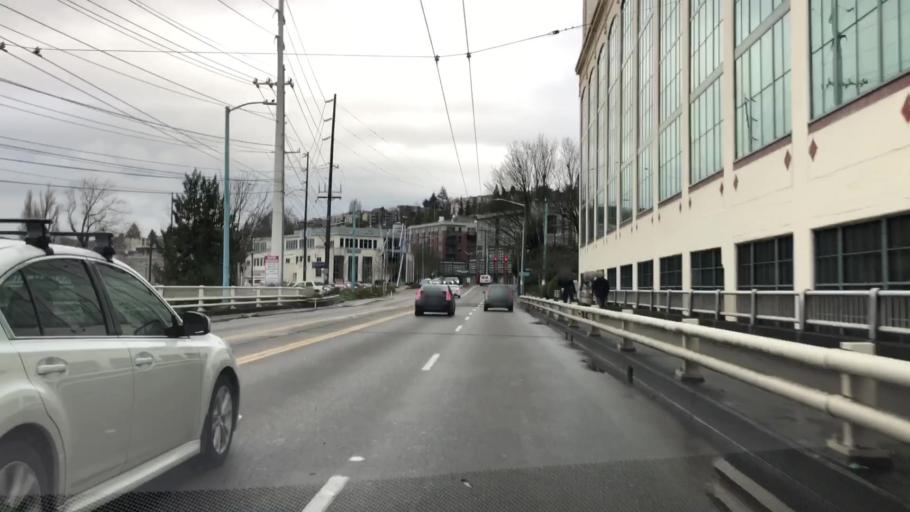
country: US
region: Washington
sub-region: King County
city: Seattle
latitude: 47.6310
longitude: -122.3278
